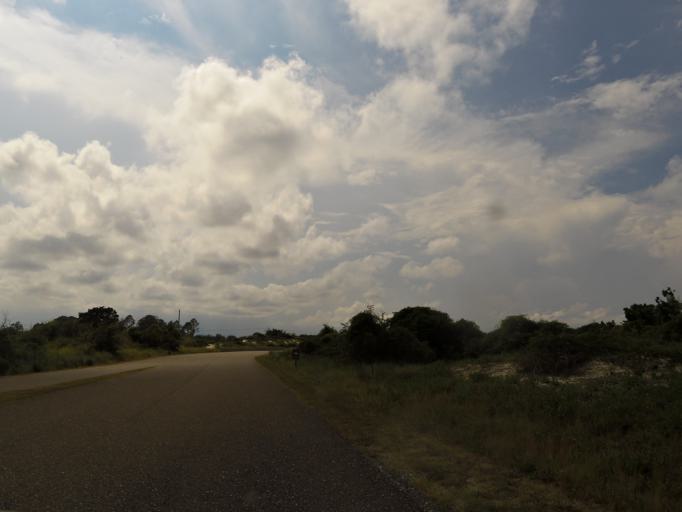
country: US
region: Florida
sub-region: Duval County
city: Atlantic Beach
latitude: 30.4369
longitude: -81.4126
